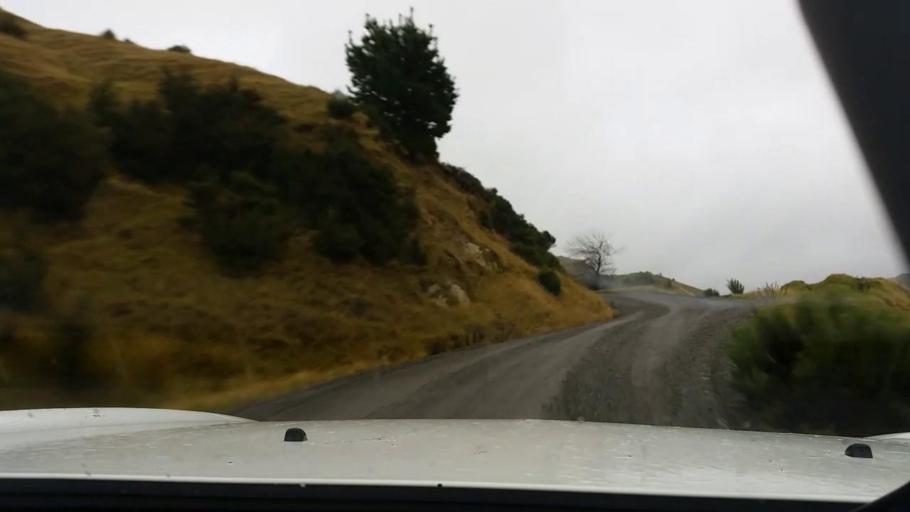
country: NZ
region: Wellington
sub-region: Masterton District
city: Masterton
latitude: -41.2500
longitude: 175.9090
